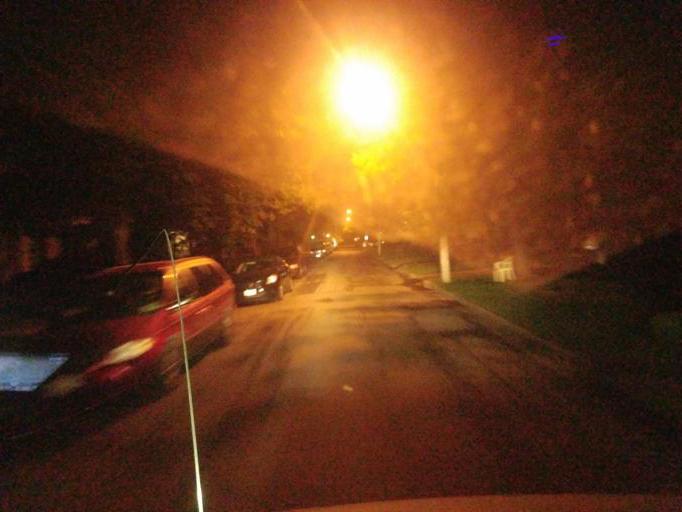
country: US
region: Ohio
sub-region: Erie County
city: Sandusky
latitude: 41.4420
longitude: -82.7124
